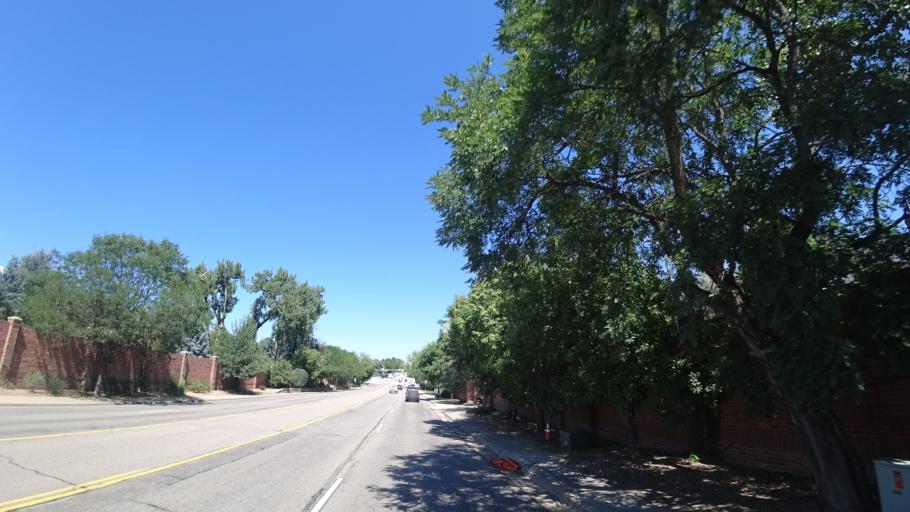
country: US
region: Colorado
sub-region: Arapahoe County
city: Greenwood Village
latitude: 39.6216
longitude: -104.9598
